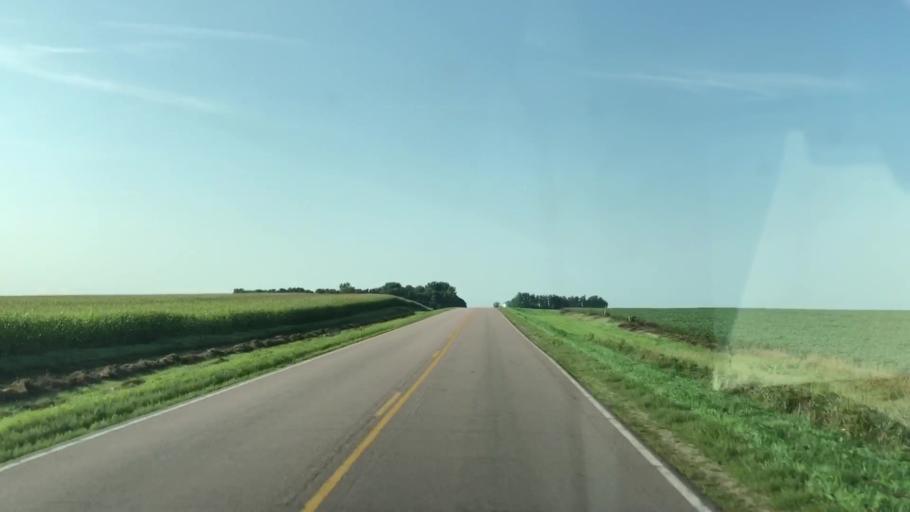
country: US
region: Iowa
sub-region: Lyon County
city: George
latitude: 43.3274
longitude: -95.9988
